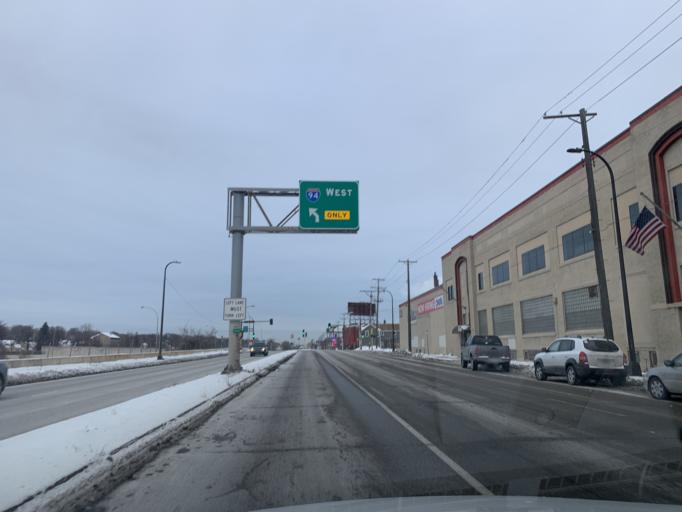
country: US
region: Minnesota
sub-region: Hennepin County
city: Minneapolis
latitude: 45.0004
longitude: -93.2818
